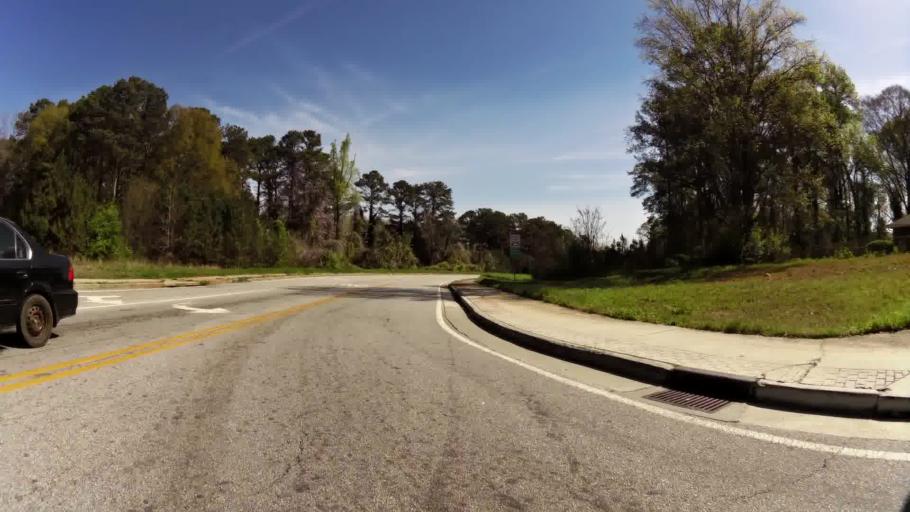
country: US
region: Georgia
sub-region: DeKalb County
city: Clarkston
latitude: 33.8272
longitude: -84.2577
